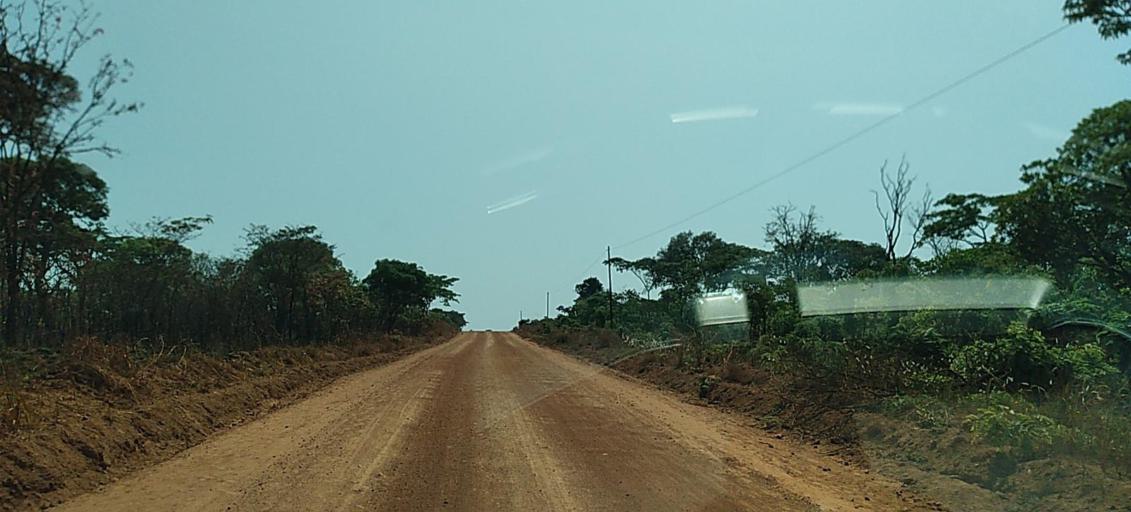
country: ZM
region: North-Western
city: Kansanshi
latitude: -11.9985
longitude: 26.5940
